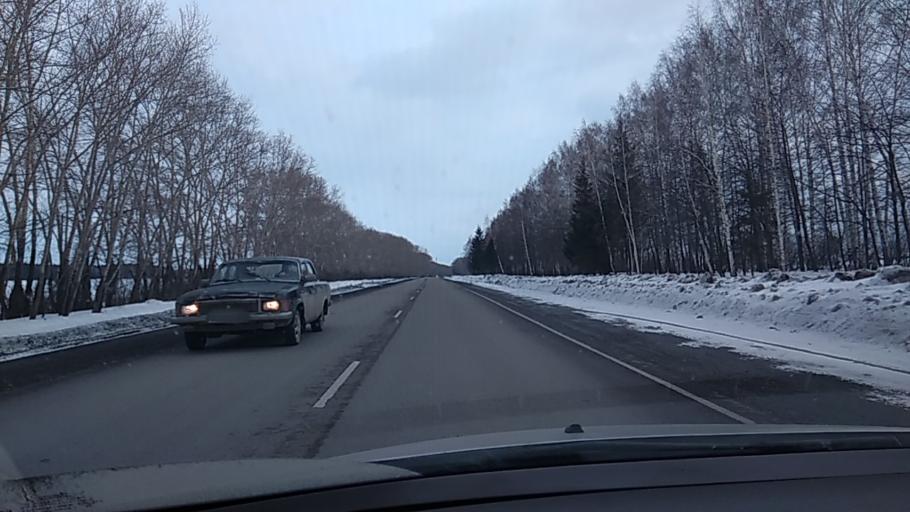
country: RU
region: Sverdlovsk
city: Dvurechensk
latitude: 56.6523
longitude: 61.1931
